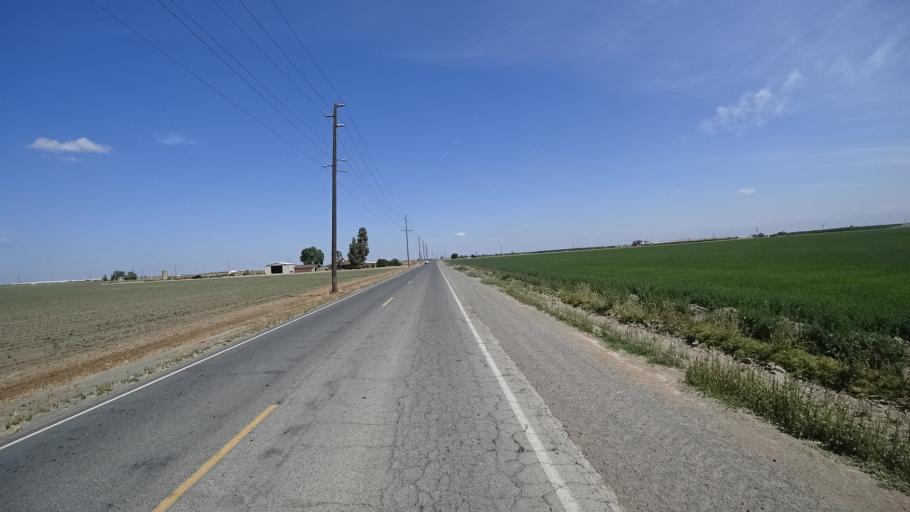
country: US
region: California
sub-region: Tulare County
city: Goshen
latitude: 36.3099
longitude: -119.4929
